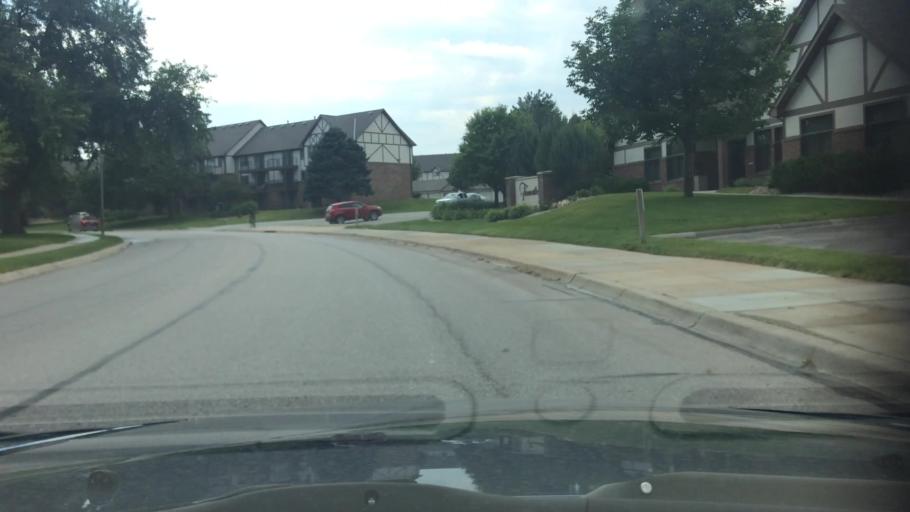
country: US
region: Nebraska
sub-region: Douglas County
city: Ralston
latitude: 41.2002
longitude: -96.0689
